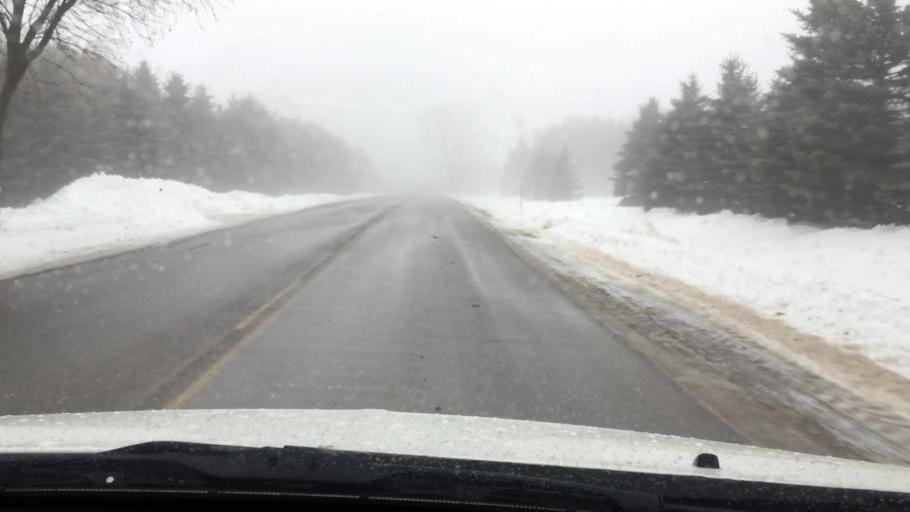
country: US
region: Michigan
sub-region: Charlevoix County
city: East Jordan
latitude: 45.1205
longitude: -85.1801
